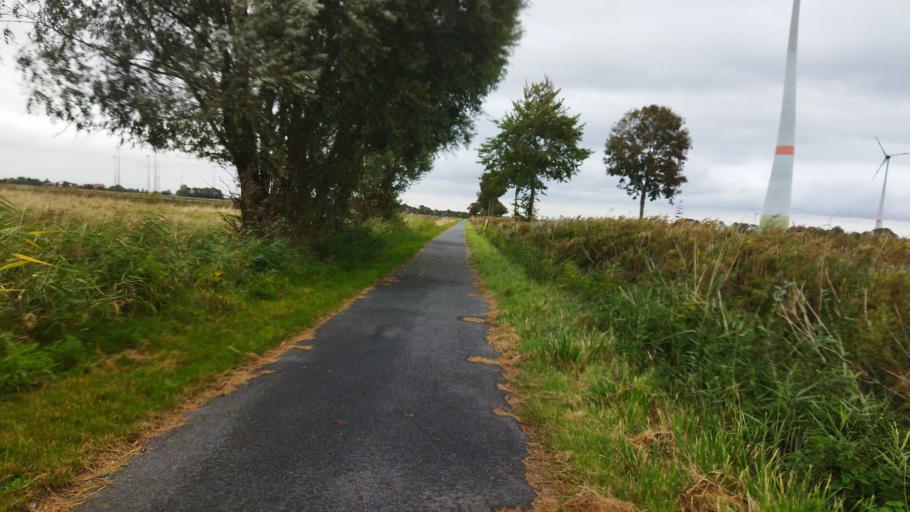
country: DE
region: Lower Saxony
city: Hinte
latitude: 53.4421
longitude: 7.1569
